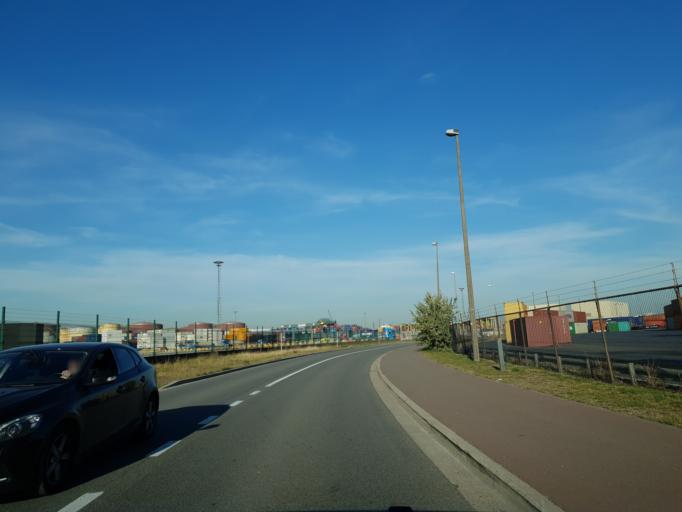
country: BE
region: Flanders
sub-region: Provincie Antwerpen
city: Stabroek
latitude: 51.3166
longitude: 4.3214
